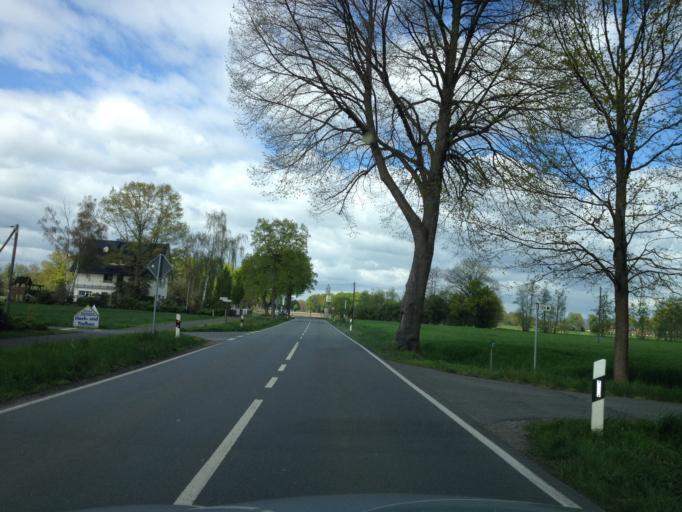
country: DE
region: North Rhine-Westphalia
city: Rietberg
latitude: 51.8532
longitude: 8.4243
